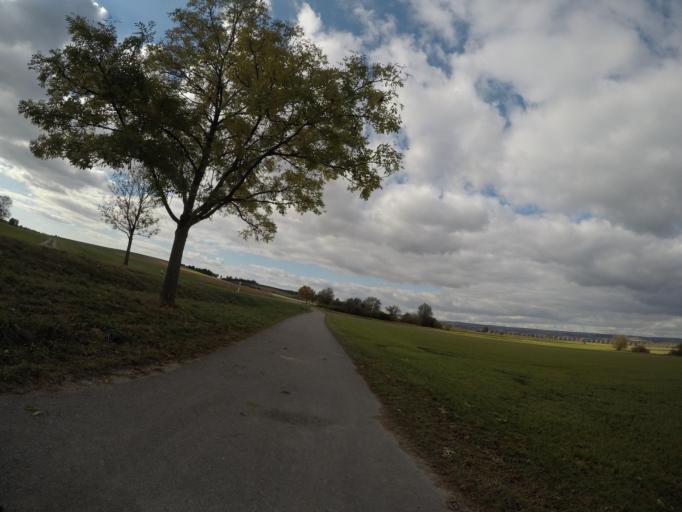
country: DE
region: Baden-Wuerttemberg
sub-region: Tuebingen Region
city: Unterstadion
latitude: 48.2076
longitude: 9.6787
